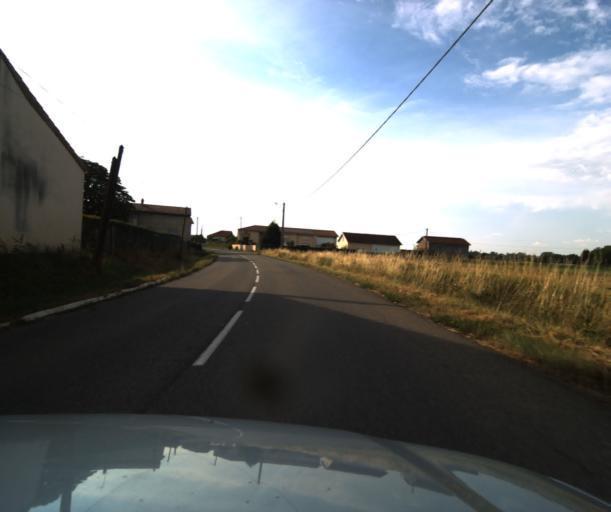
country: FR
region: Midi-Pyrenees
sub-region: Departement du Tarn-et-Garonne
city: Castelsarrasin
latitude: 44.0224
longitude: 1.1118
